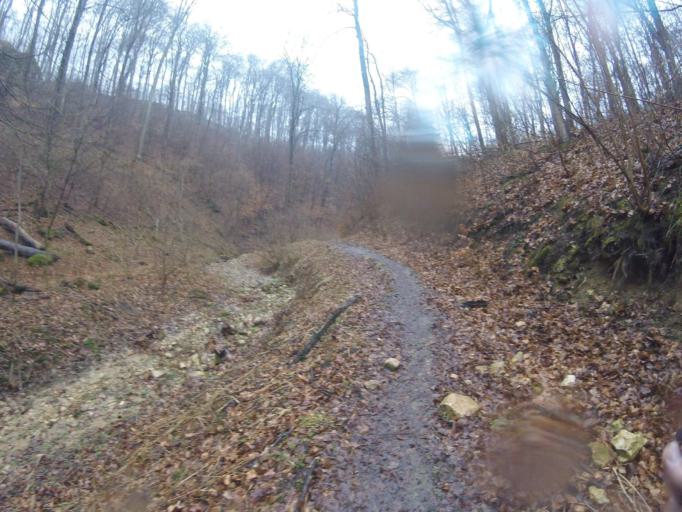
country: HU
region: Veszprem
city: Zirc
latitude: 47.3369
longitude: 17.8917
